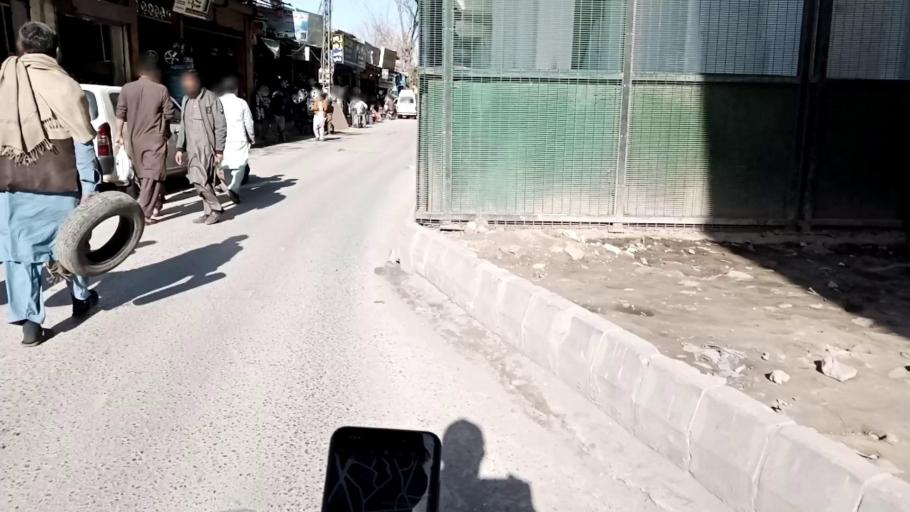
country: PK
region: Khyber Pakhtunkhwa
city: Peshawar
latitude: 34.0043
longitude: 71.5556
